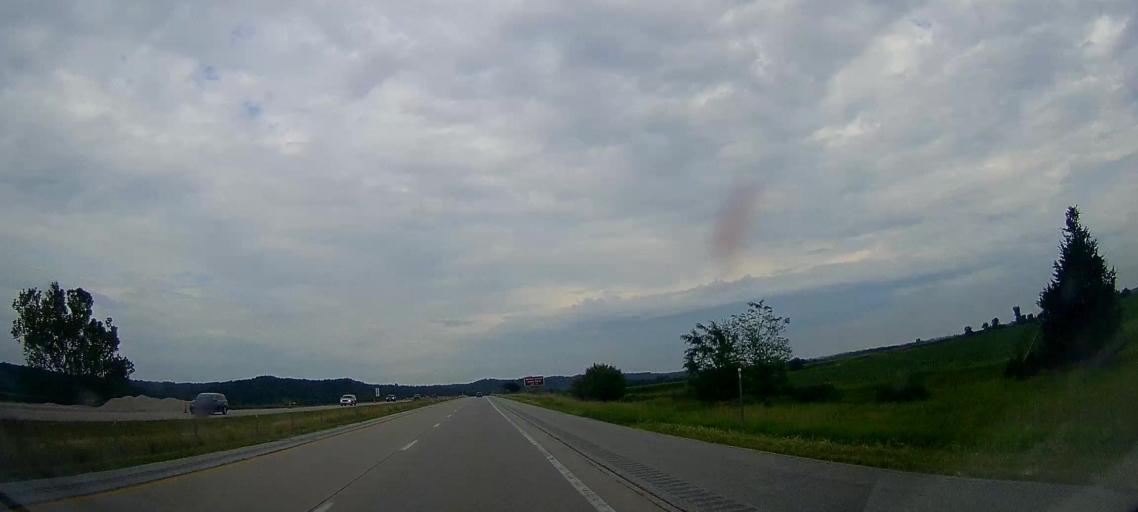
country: US
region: Iowa
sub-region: Harrison County
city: Missouri Valley
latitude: 41.5105
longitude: -95.9089
